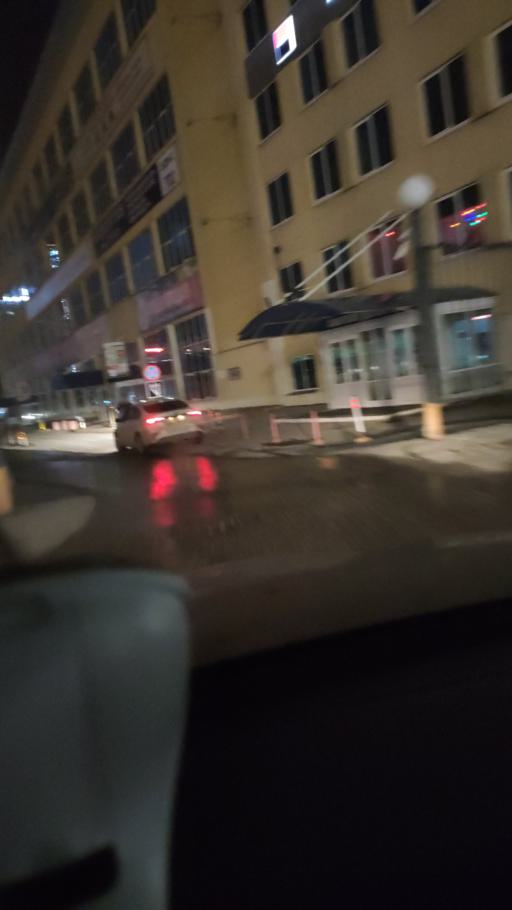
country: RU
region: Samara
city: Samara
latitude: 53.2149
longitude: 50.1286
